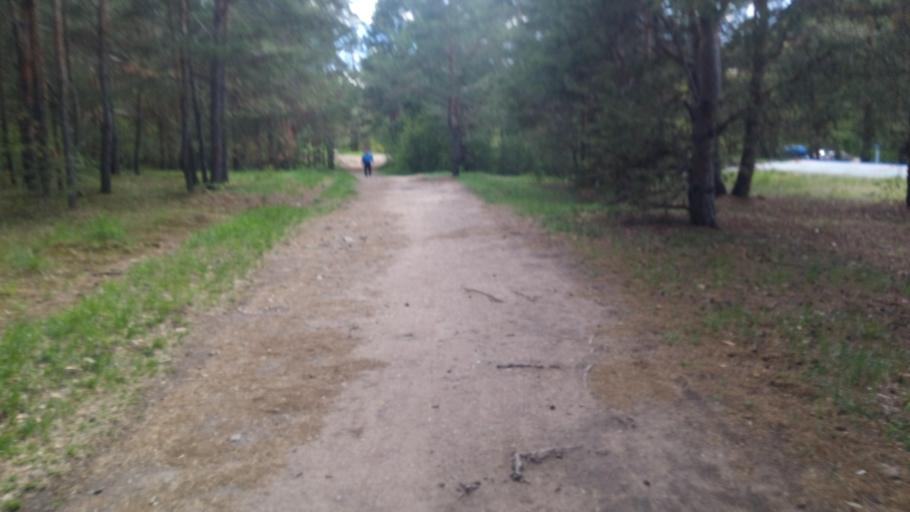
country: RU
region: Chelyabinsk
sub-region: Gorod Chelyabinsk
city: Chelyabinsk
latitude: 55.1674
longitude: 61.3439
